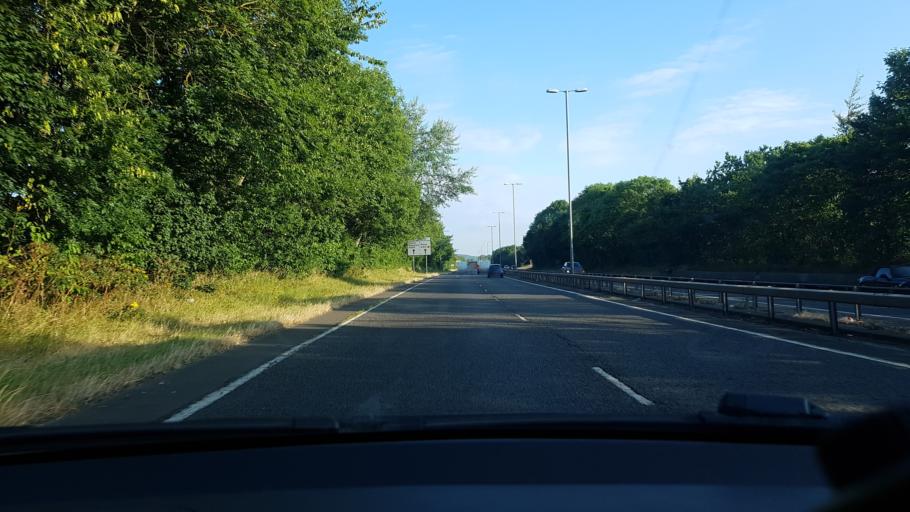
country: GB
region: England
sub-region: Nottinghamshire
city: Eastwood
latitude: 53.0106
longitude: -1.3138
